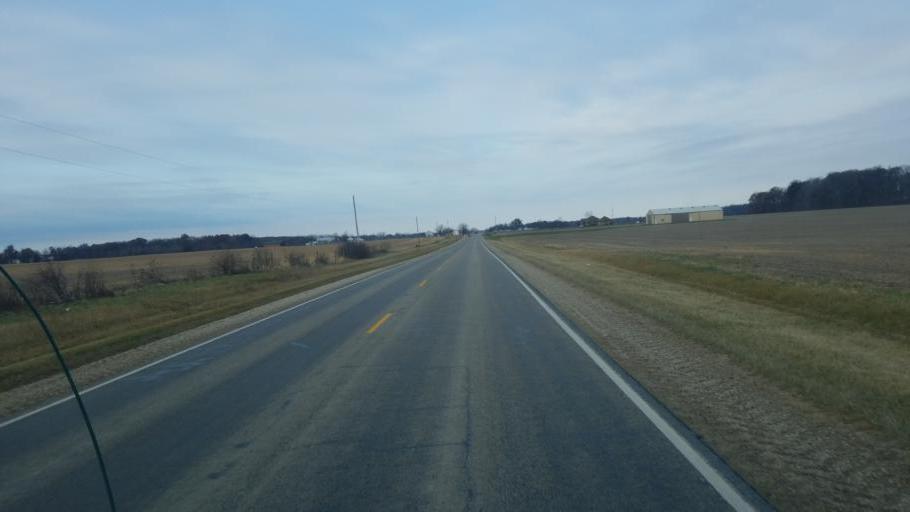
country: US
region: Indiana
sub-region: Adams County
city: Geneva
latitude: 40.5422
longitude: -84.8848
